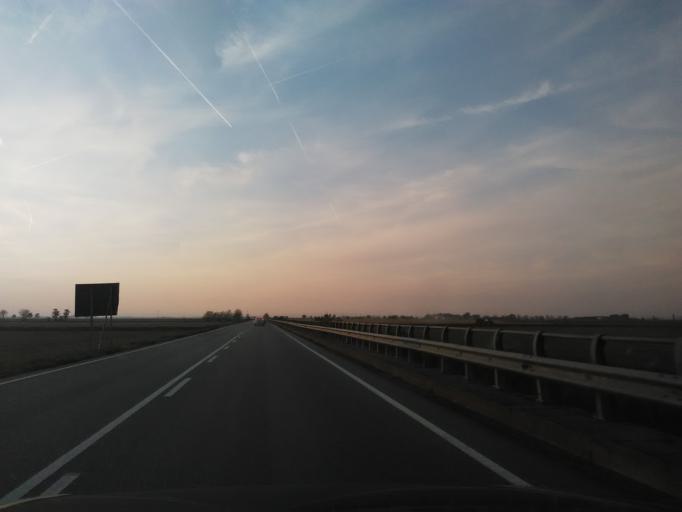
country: IT
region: Piedmont
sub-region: Provincia di Vercelli
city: Sali Vercellese
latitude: 45.3286
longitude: 8.3262
